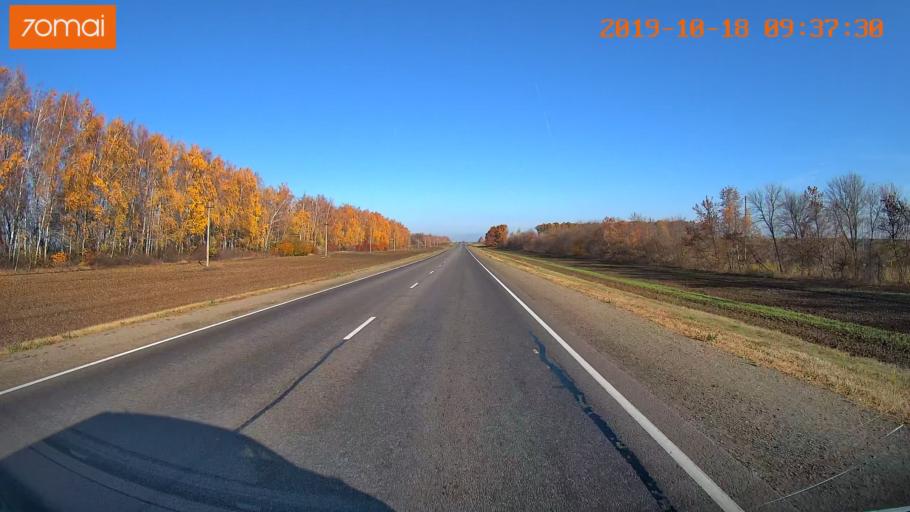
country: RU
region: Tula
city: Yefremov
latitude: 53.2234
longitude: 38.1408
